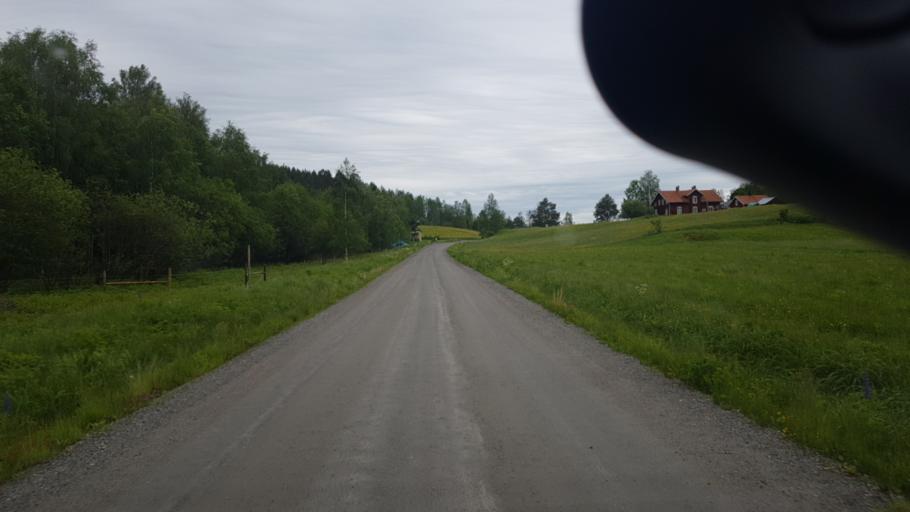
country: NO
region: Ostfold
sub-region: Romskog
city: Romskog
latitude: 59.6712
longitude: 11.9331
